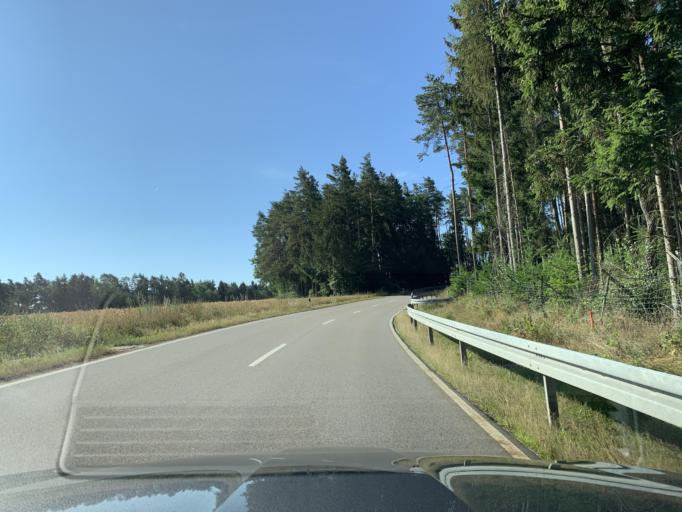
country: DE
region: Bavaria
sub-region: Upper Palatinate
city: Schwarzhofen
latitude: 49.3705
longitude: 12.3298
